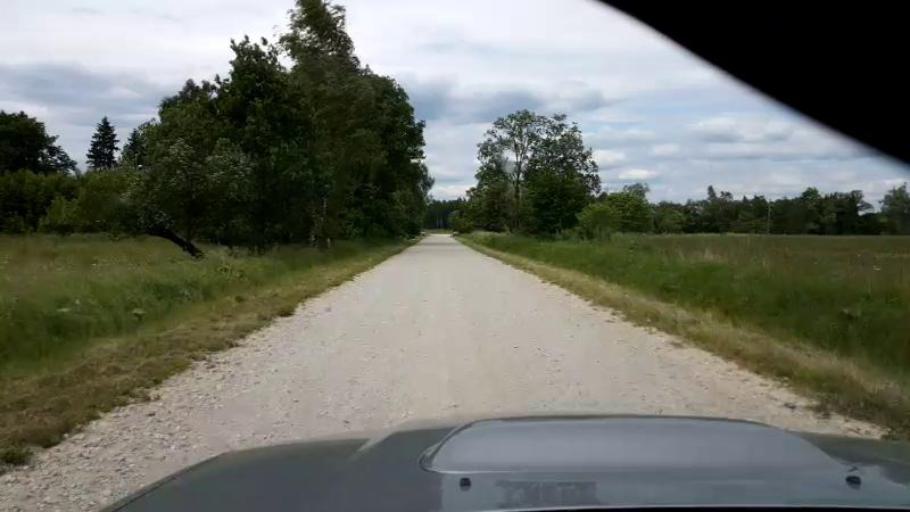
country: EE
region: Paernumaa
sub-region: Sauga vald
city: Sauga
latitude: 58.5135
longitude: 24.5807
